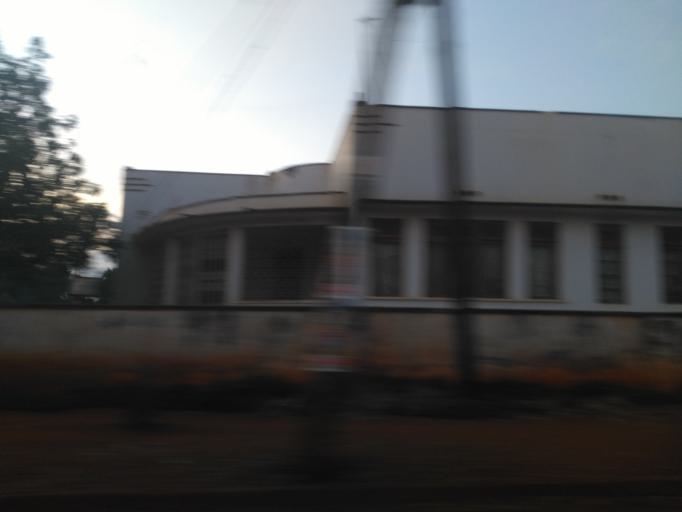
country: UG
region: Eastern Region
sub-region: Jinja District
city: Jinja
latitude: 0.4325
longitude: 33.2077
